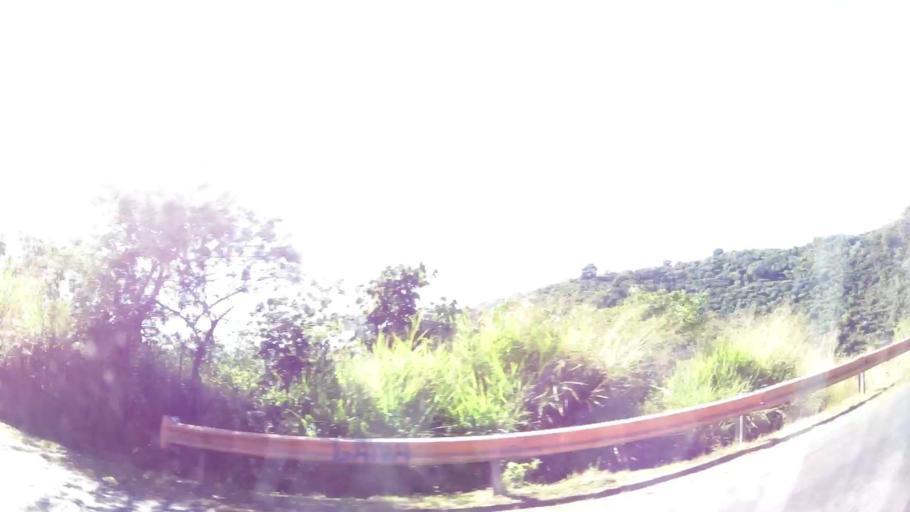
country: SV
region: Ahuachapan
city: Concepcion de Ataco
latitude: 13.8751
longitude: -89.8421
